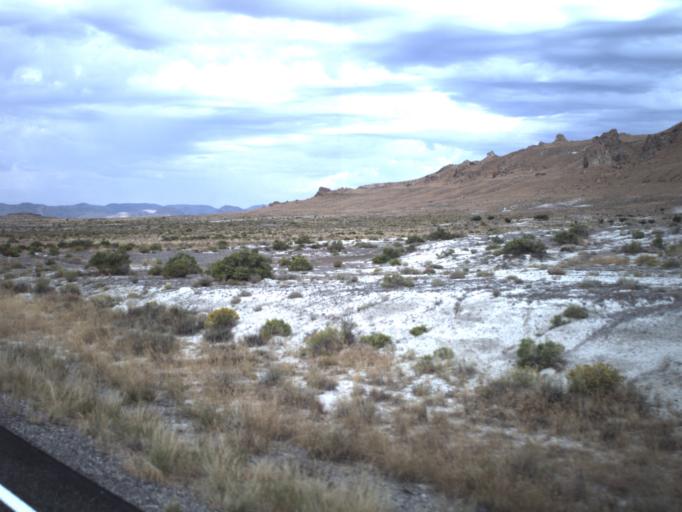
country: US
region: Utah
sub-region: Tooele County
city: Wendover
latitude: 41.4279
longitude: -113.8291
